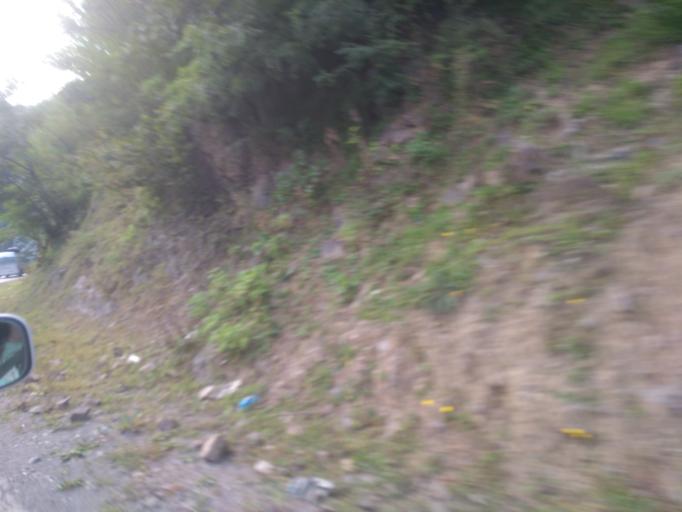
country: TR
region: Artvin
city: Muratli
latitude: 41.5459
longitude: 41.7538
